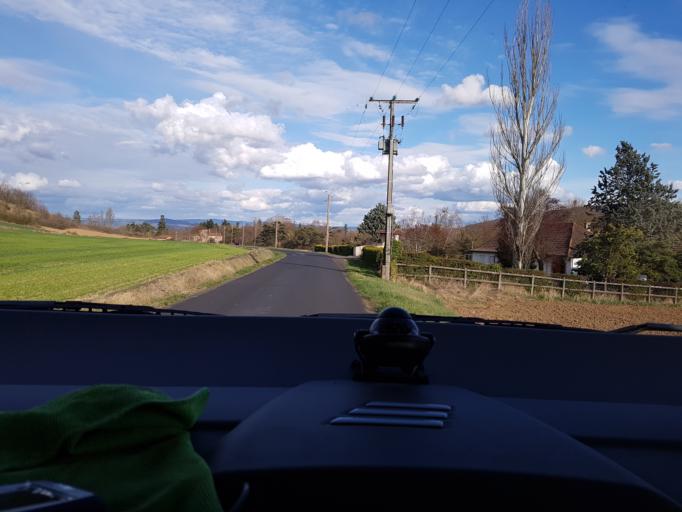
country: FR
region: Auvergne
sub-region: Departement du Puy-de-Dome
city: Saint-Germain-Lembron
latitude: 45.4526
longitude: 3.2002
